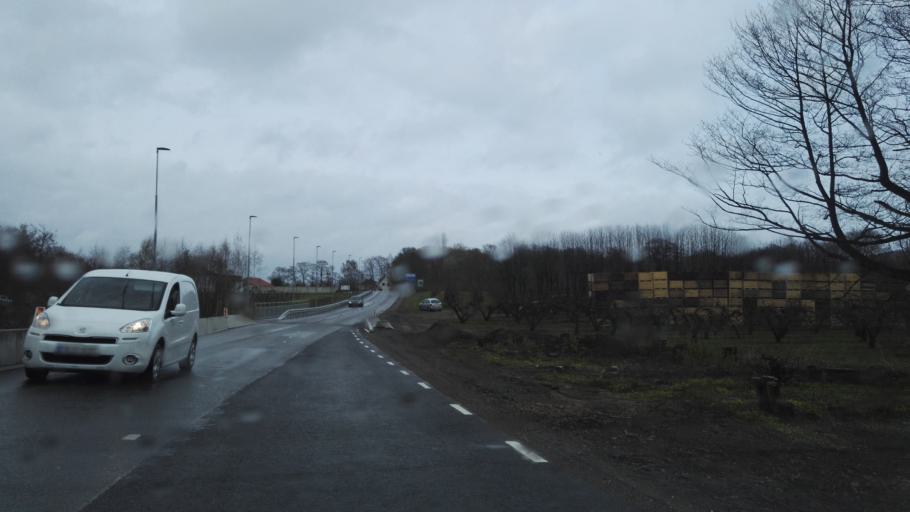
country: SE
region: Skane
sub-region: Simrishamns Kommun
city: Kivik
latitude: 55.6743
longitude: 14.2237
